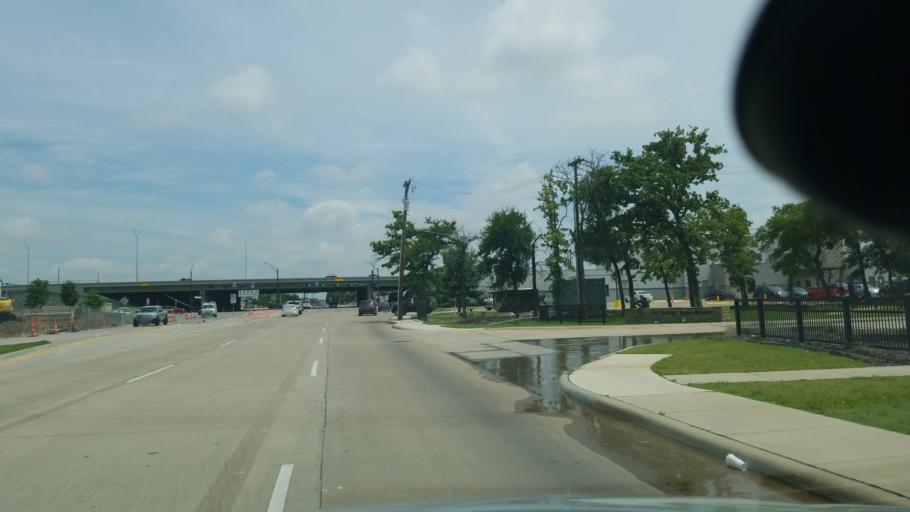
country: US
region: Texas
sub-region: Dallas County
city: Irving
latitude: 32.8347
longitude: -96.9591
